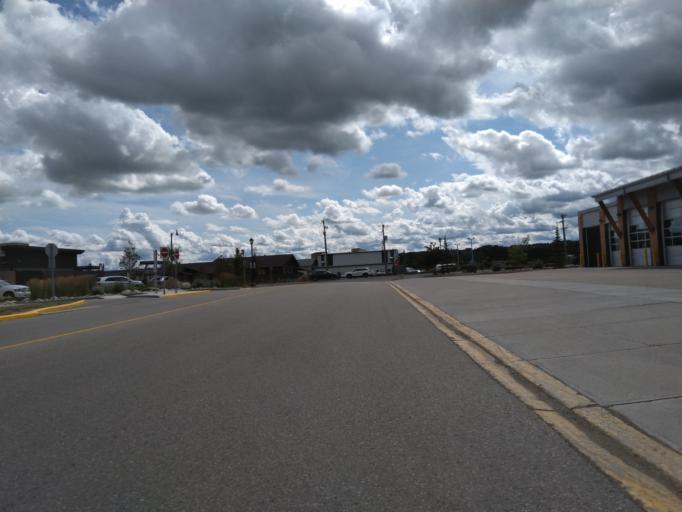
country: CA
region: Alberta
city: Cochrane
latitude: 51.1841
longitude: -114.4732
